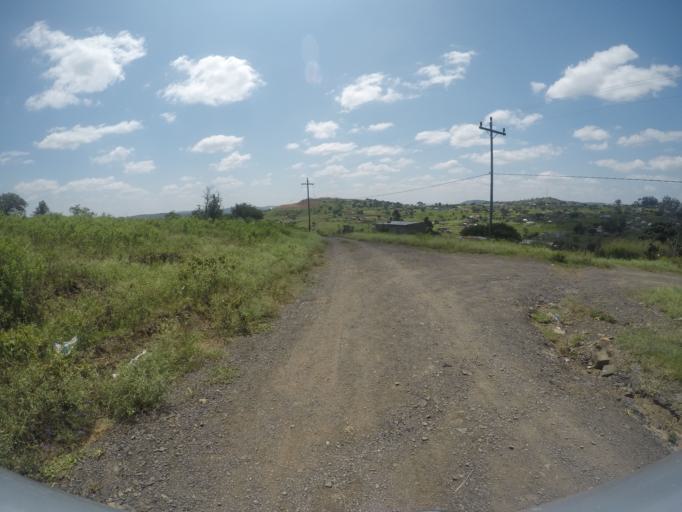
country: ZA
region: KwaZulu-Natal
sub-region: uThungulu District Municipality
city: Empangeni
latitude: -28.6042
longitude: 31.7355
